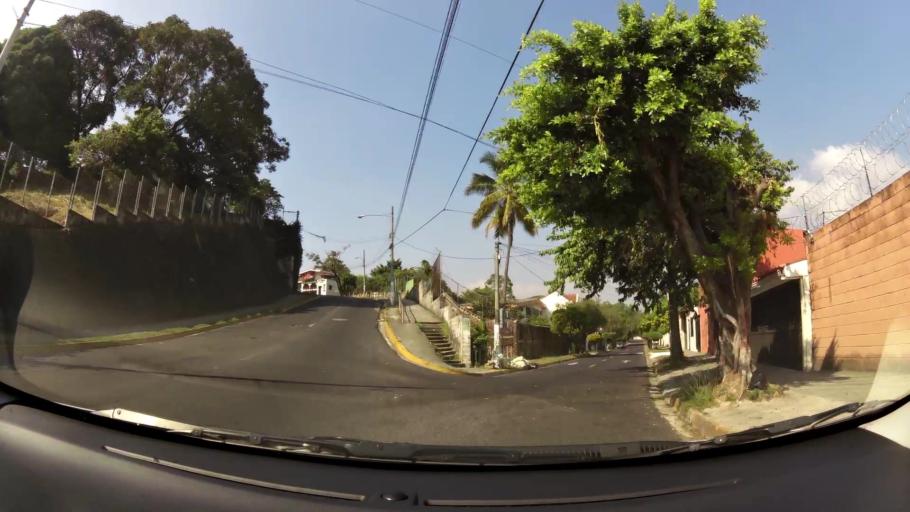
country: SV
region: La Libertad
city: Antiguo Cuscatlan
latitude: 13.6743
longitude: -89.2374
